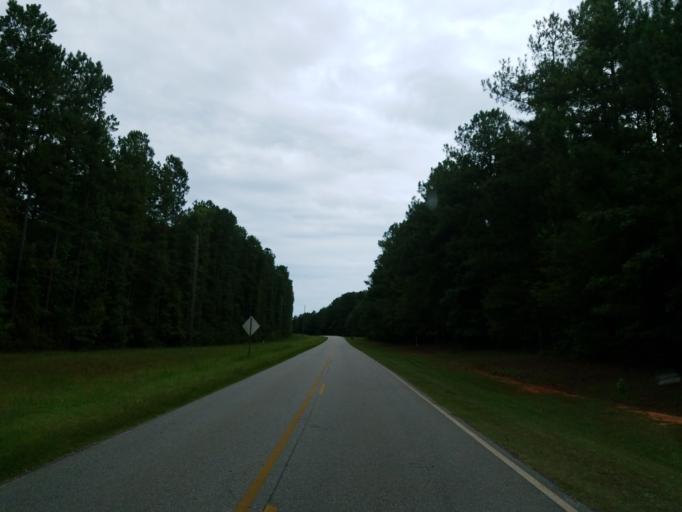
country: US
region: Georgia
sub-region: Monroe County
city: Forsyth
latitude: 32.9446
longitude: -83.9455
